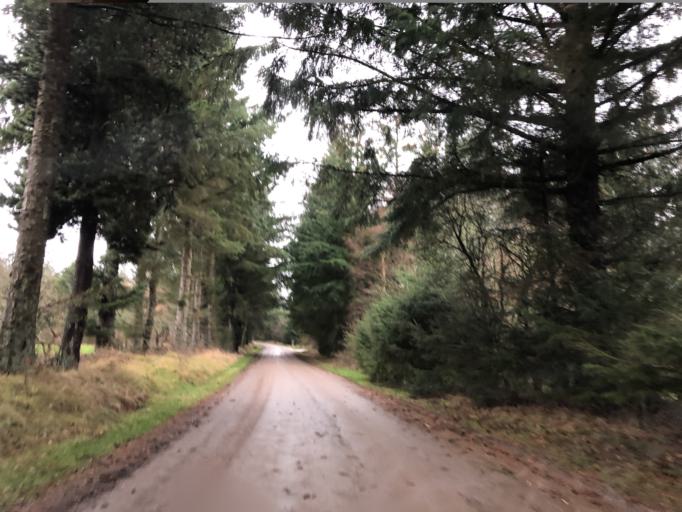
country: DK
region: Central Jutland
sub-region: Holstebro Kommune
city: Ulfborg
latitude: 56.2784
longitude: 8.1591
